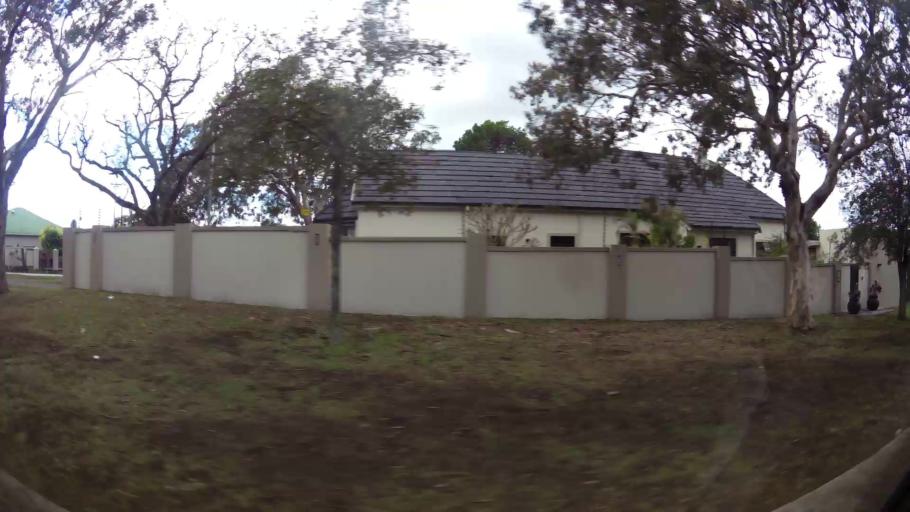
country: ZA
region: Eastern Cape
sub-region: Nelson Mandela Bay Metropolitan Municipality
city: Port Elizabeth
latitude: -33.9656
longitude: 25.5904
